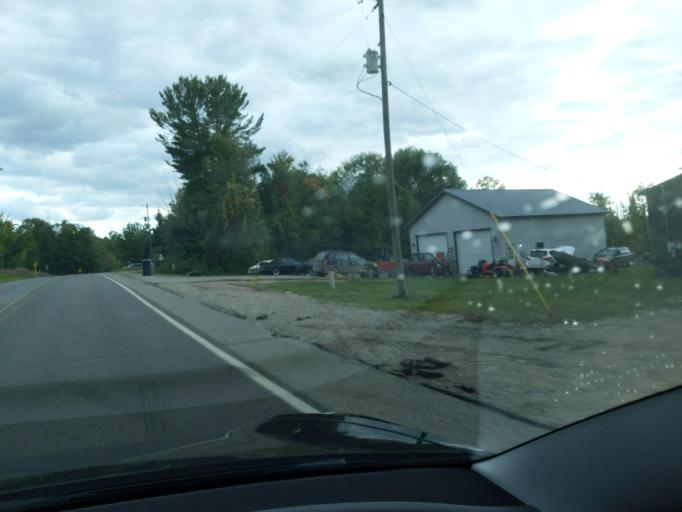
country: US
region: Michigan
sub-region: Kalkaska County
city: Rapid City
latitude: 44.7961
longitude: -85.2725
